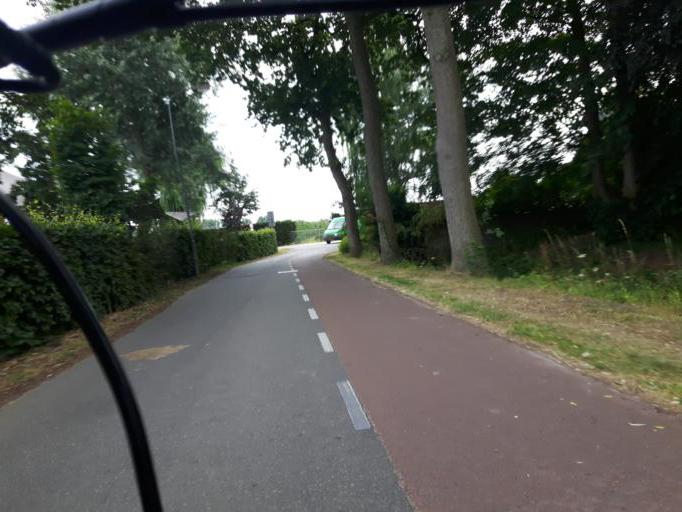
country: NL
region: Gelderland
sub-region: Gemeente Tiel
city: Tiel
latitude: 51.8802
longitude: 5.3753
